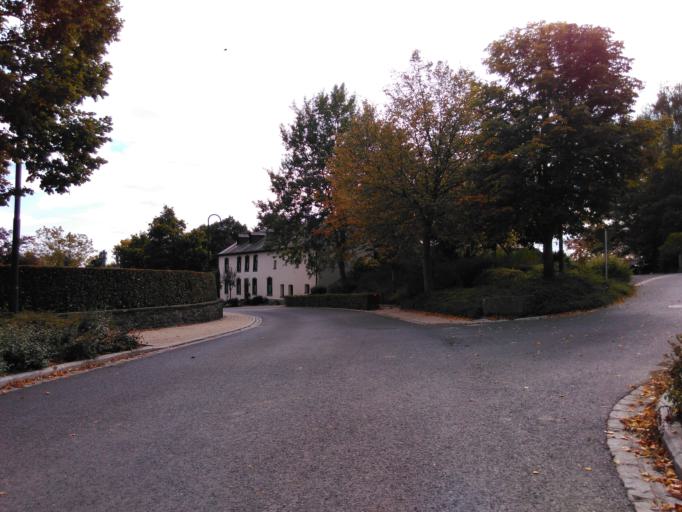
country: LU
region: Diekirch
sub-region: Canton de Clervaux
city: Troisvierges
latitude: 50.1459
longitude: 5.9819
